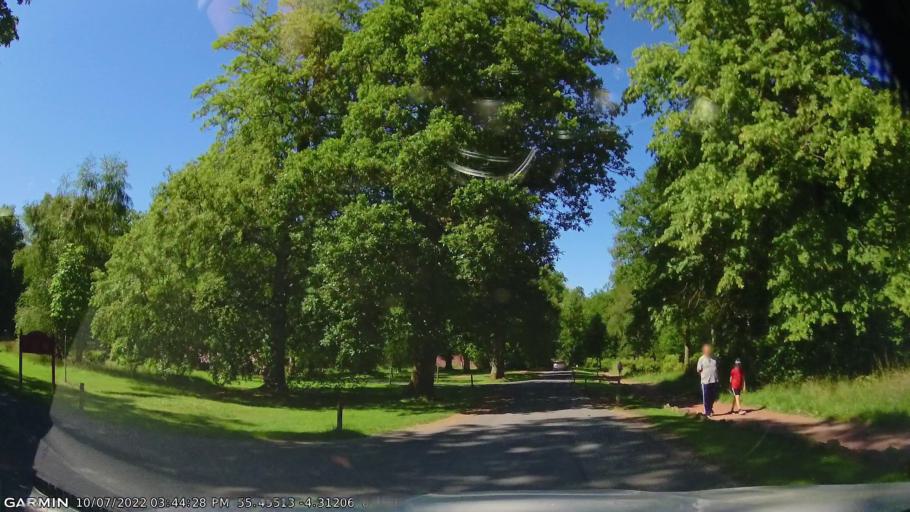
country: GB
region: Scotland
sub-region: East Ayrshire
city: Auchinleck
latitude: 55.4550
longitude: -4.3118
